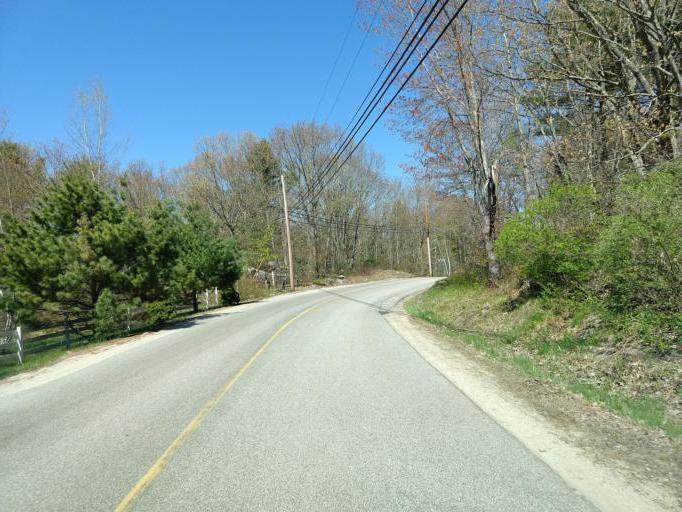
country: US
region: Maine
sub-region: York County
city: Arundel
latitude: 43.3893
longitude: -70.4604
